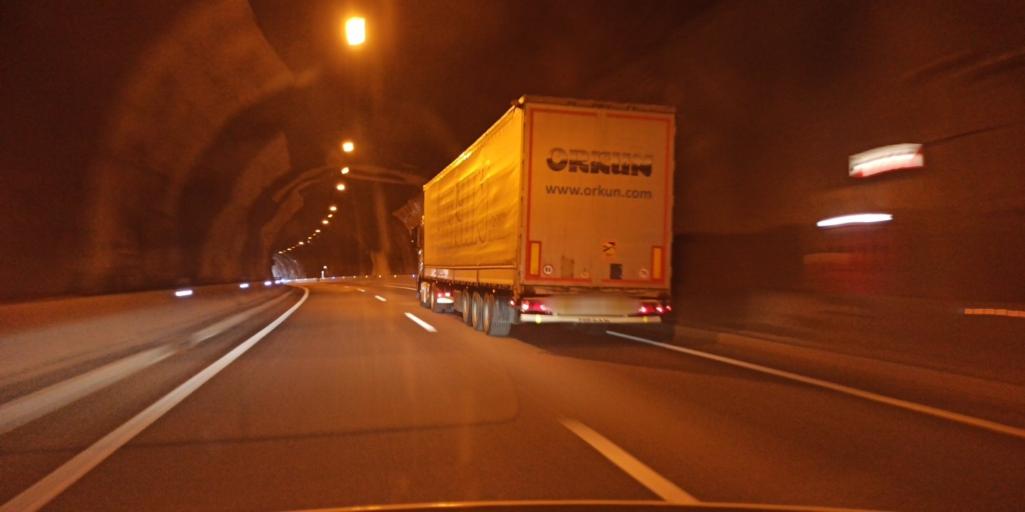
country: ES
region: Catalonia
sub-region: Provincia de Barcelona
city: Muntanyola
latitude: 41.9158
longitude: 2.1344
